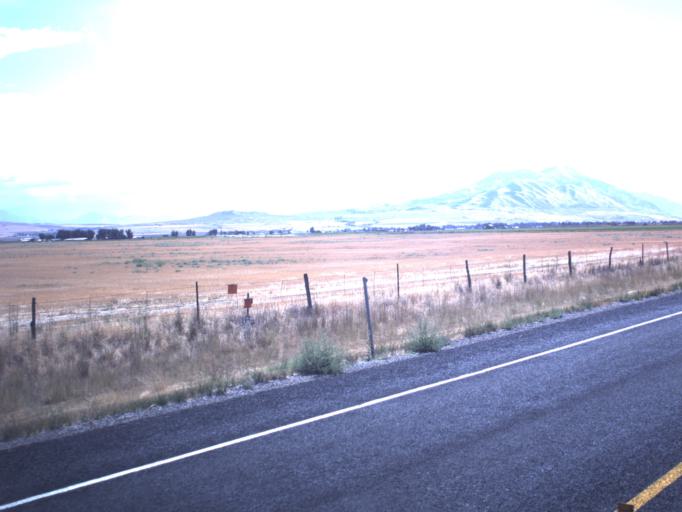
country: US
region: Utah
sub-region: Box Elder County
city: Garland
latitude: 41.8544
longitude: -112.1465
